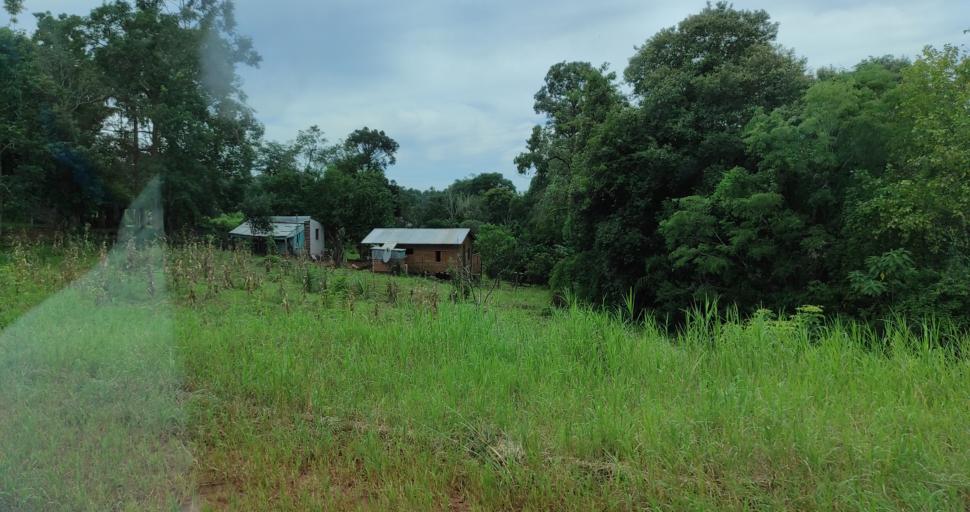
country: AR
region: Misiones
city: El Alcazar
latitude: -26.7204
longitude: -54.8137
